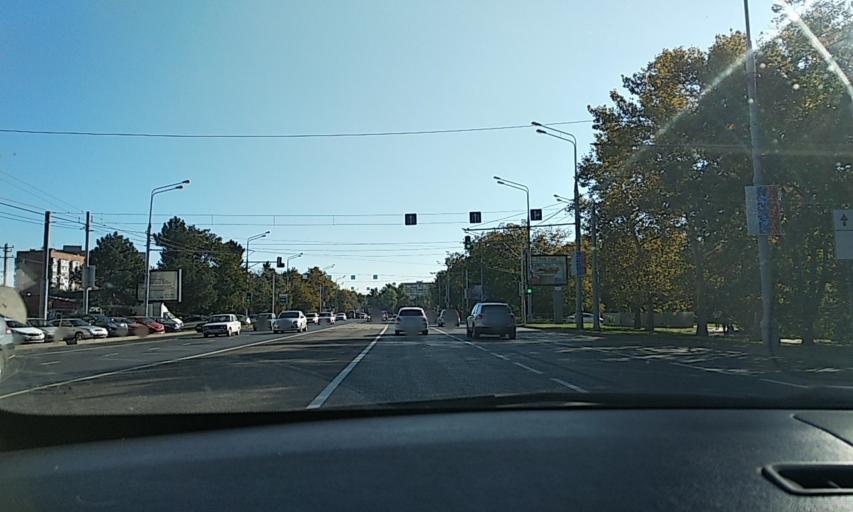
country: RU
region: Krasnodarskiy
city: Pashkovskiy
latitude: 45.0125
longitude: 39.0713
